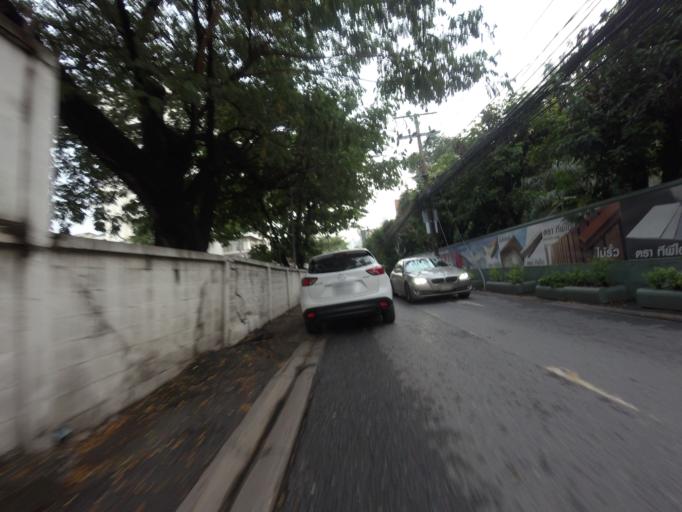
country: TH
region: Bangkok
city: Watthana
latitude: 13.7368
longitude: 100.5769
